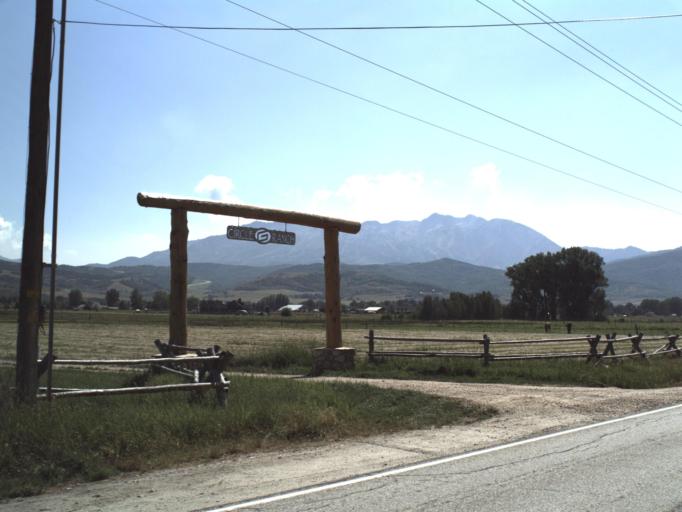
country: US
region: Utah
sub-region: Weber County
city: Wolf Creek
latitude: 41.2621
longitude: -111.7437
